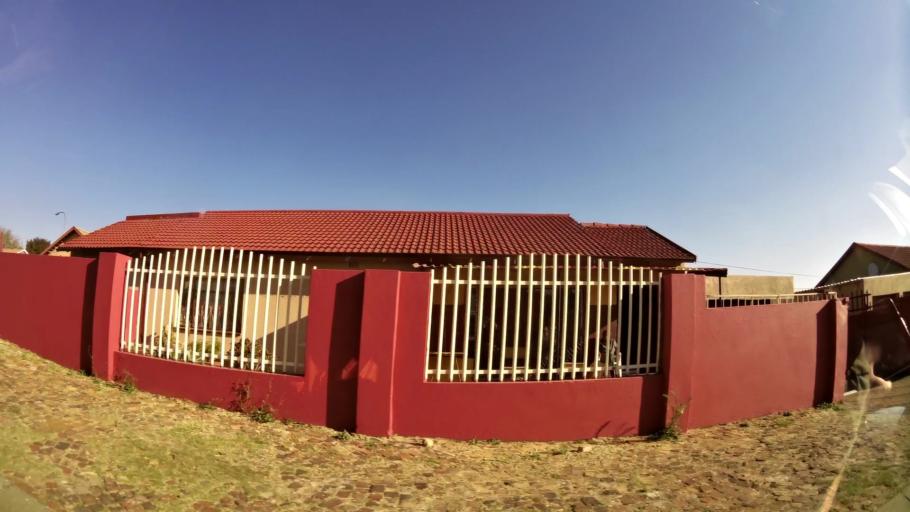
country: ZA
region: Gauteng
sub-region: City of Johannesburg Metropolitan Municipality
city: Johannesburg
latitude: -26.2124
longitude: 27.9786
